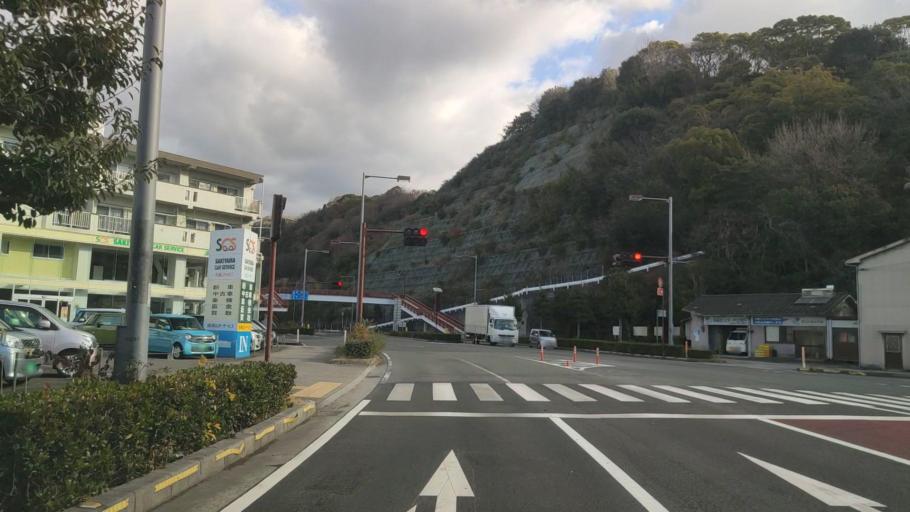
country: JP
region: Ehime
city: Masaki-cho
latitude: 33.8314
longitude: 132.7085
